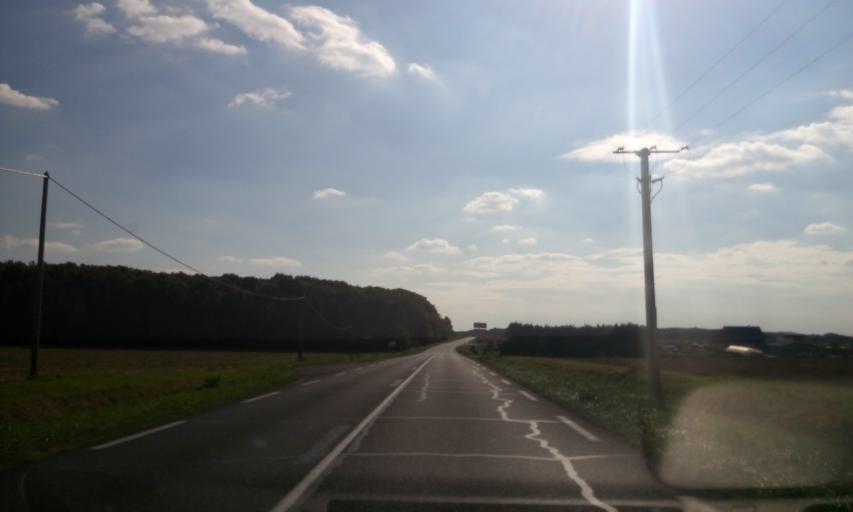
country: FR
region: Centre
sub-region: Departement d'Indre-et-Loire
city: Poce-sur-Cisse
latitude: 47.4812
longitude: 1.0082
